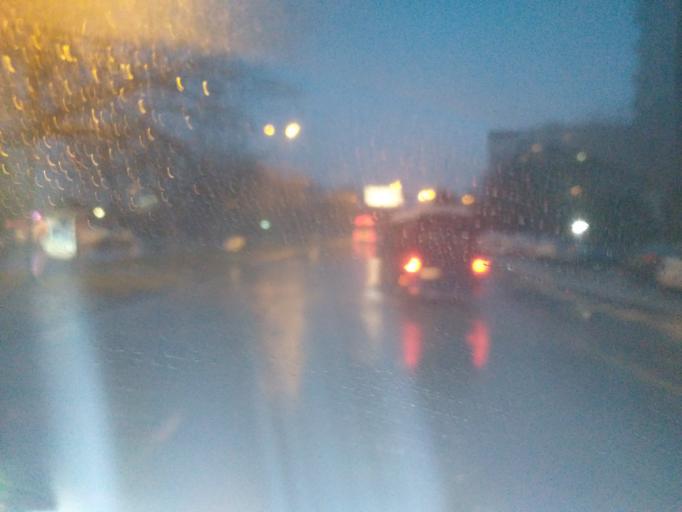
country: TR
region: Ankara
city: Ankara
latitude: 39.9440
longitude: 32.8254
